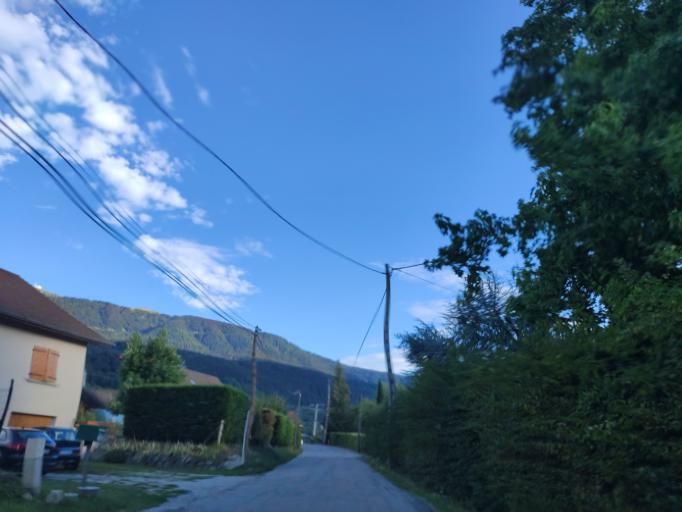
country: FR
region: Rhone-Alpes
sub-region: Departement de l'Isere
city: Revel
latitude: 45.1591
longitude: 5.8524
